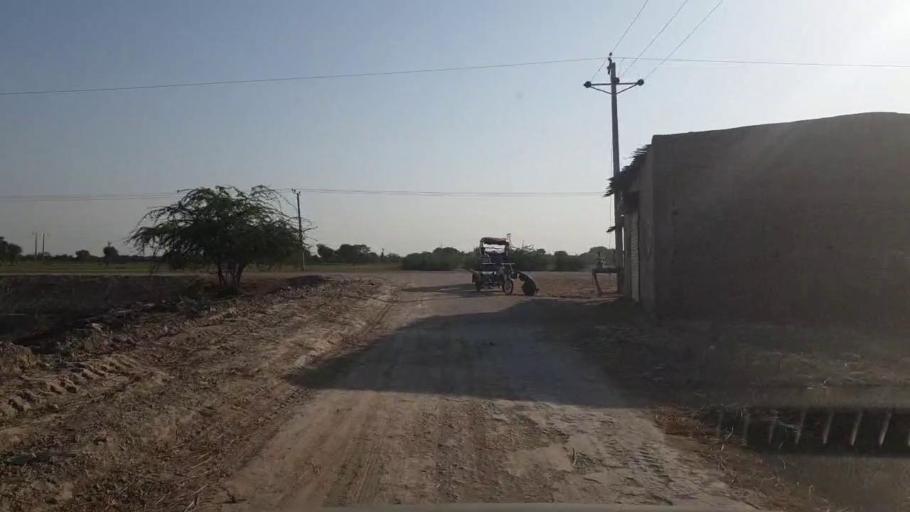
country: PK
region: Sindh
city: Talhar
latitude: 24.9077
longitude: 68.7422
